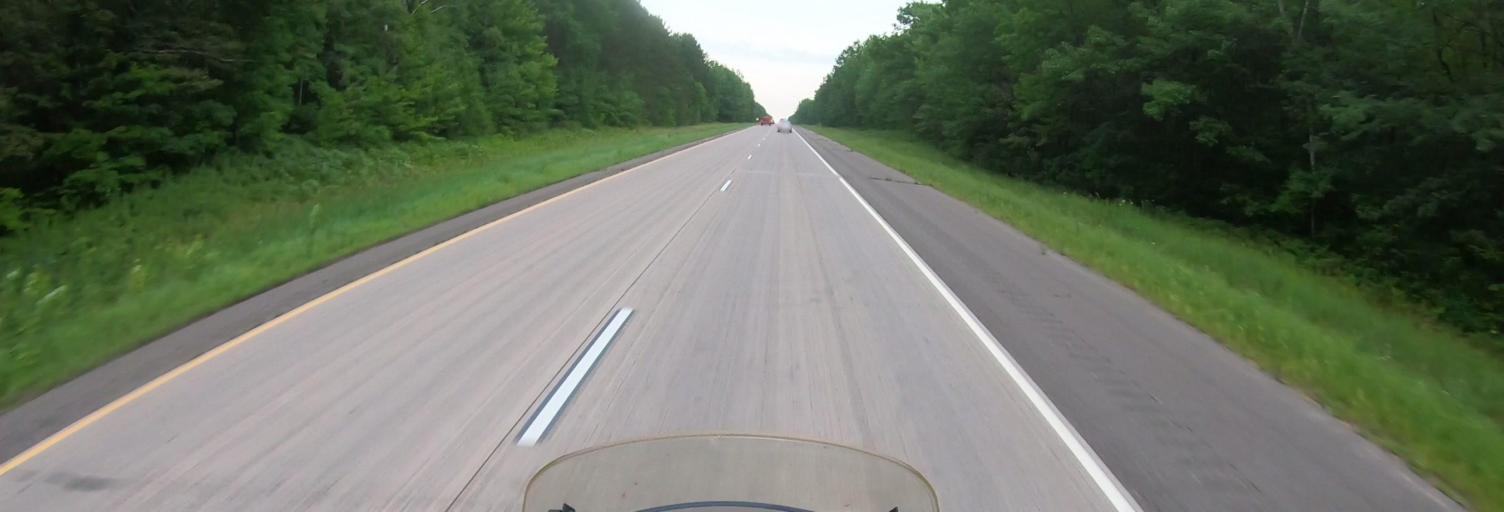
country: US
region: Minnesota
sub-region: Pine County
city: Hinckley
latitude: 46.0691
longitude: -92.9046
